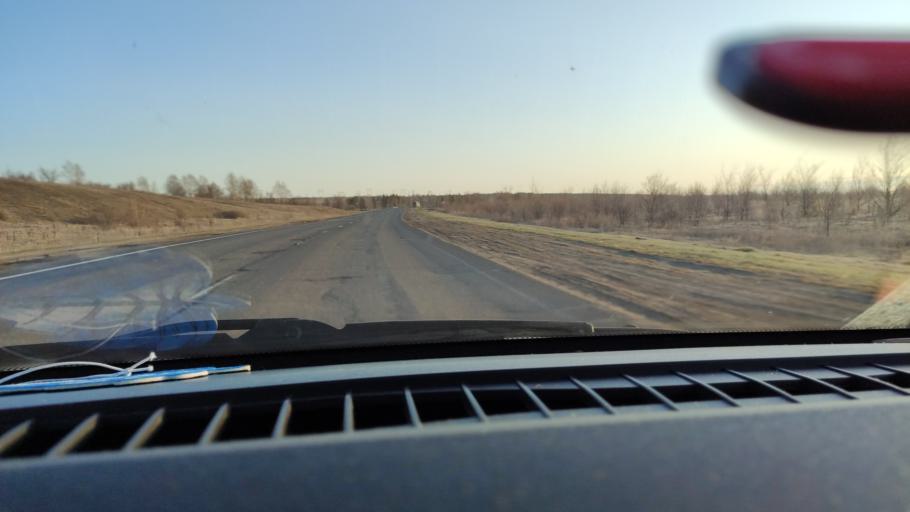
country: RU
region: Saratov
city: Sennoy
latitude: 52.0980
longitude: 46.8133
